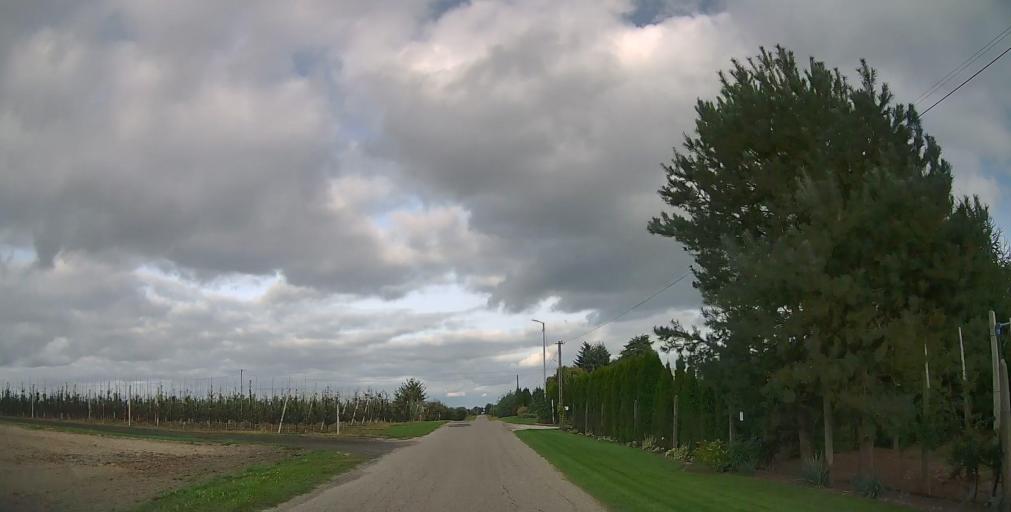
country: PL
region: Masovian Voivodeship
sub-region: Powiat grojecki
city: Jasieniec
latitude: 51.7697
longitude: 20.9087
